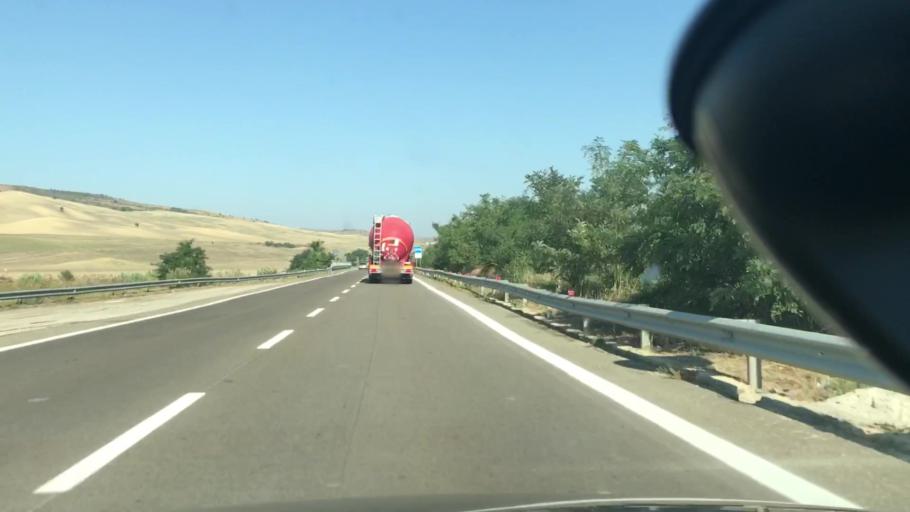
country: IT
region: Basilicate
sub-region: Provincia di Matera
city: Irsina
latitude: 40.7908
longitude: 16.2838
